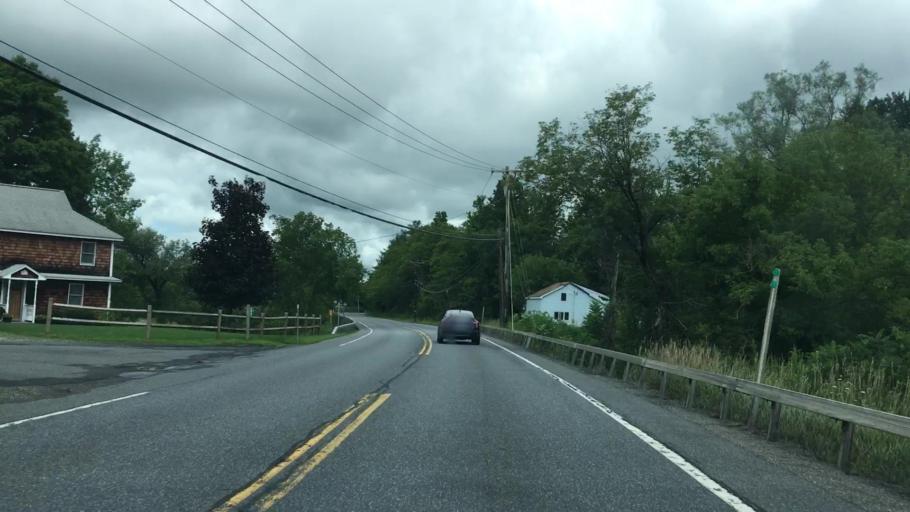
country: US
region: New York
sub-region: Rensselaer County
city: Hoosick Falls
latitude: 42.8354
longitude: -73.4843
